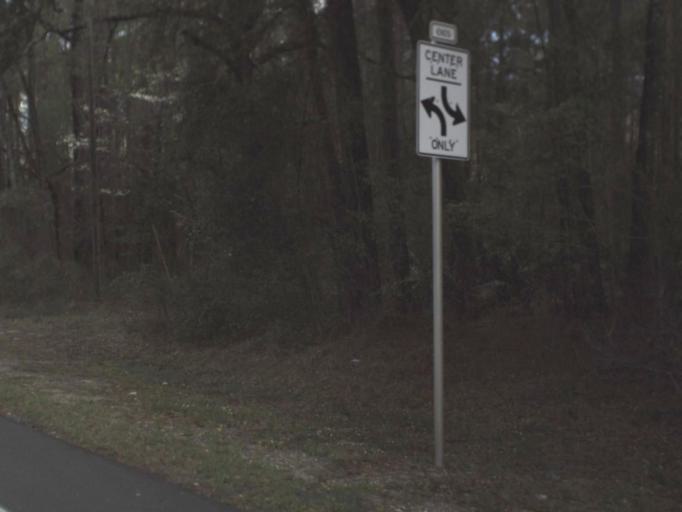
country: US
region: Florida
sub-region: Leon County
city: Woodville
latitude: 30.2880
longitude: -84.3523
